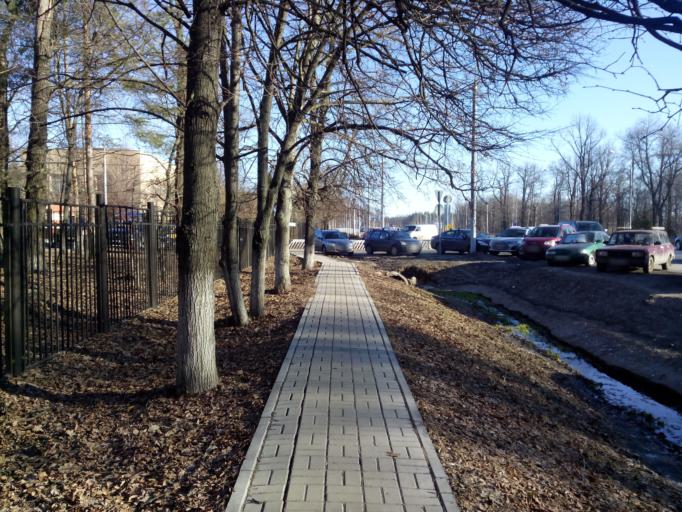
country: RU
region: Moskovskaya
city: Odintsovo
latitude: 55.6848
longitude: 37.2715
